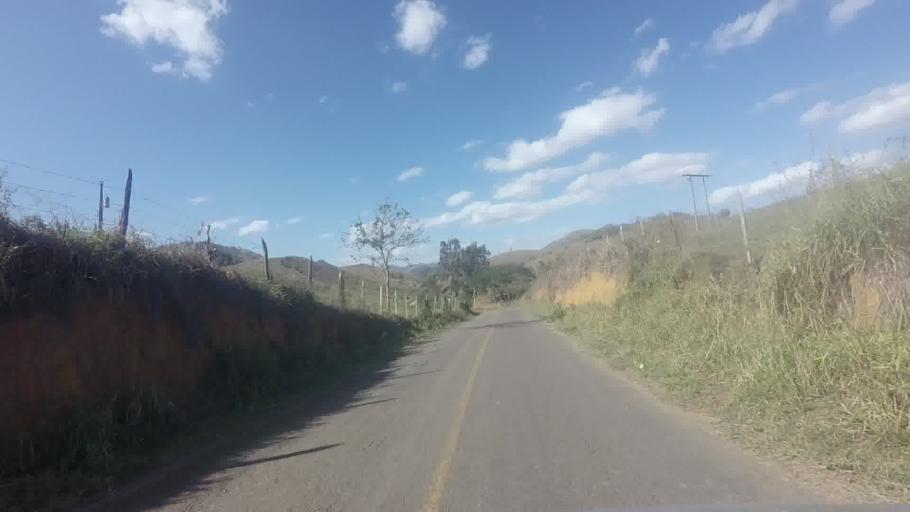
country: BR
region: Rio de Janeiro
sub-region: Bom Jesus Do Itabapoana
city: Bom Jesus do Itabapoana
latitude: -21.1119
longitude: -41.6501
